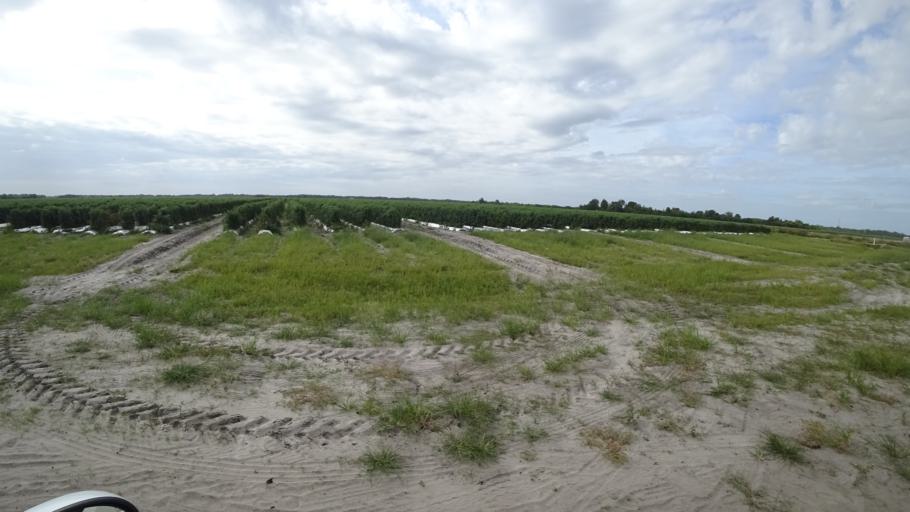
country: US
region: Florida
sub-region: Hillsborough County
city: Wimauma
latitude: 27.5922
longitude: -82.3100
